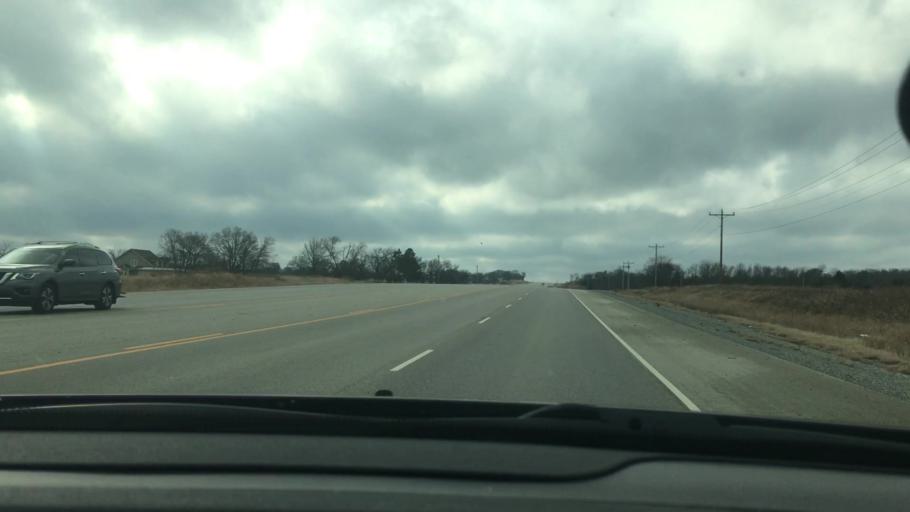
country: US
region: Oklahoma
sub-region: Bryan County
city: Durant
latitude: 34.0662
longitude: -96.3730
